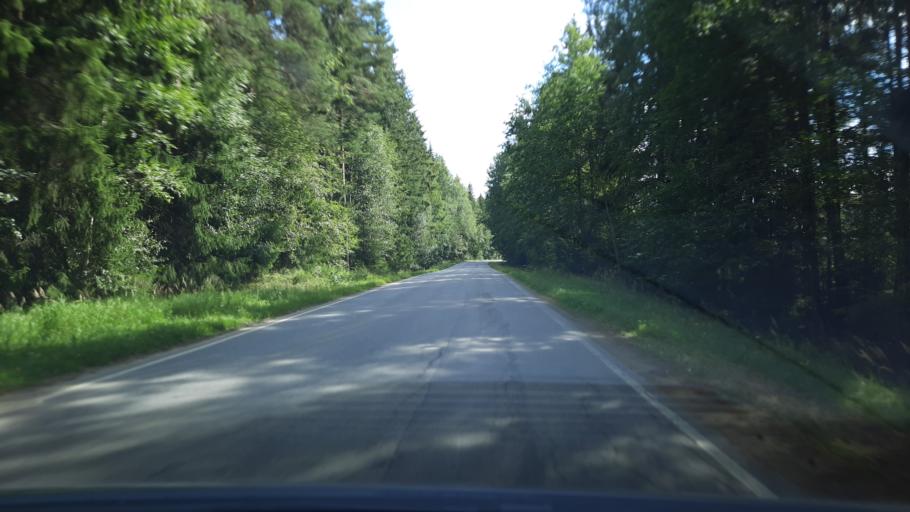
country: FI
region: Pirkanmaa
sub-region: Etelae-Pirkanmaa
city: Urjala
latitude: 61.1786
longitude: 23.3564
